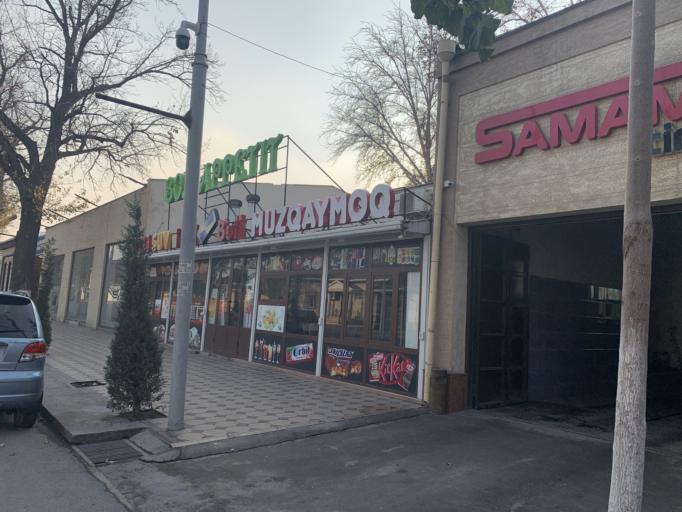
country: UZ
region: Fergana
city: Qo`qon
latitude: 40.5351
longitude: 70.9373
